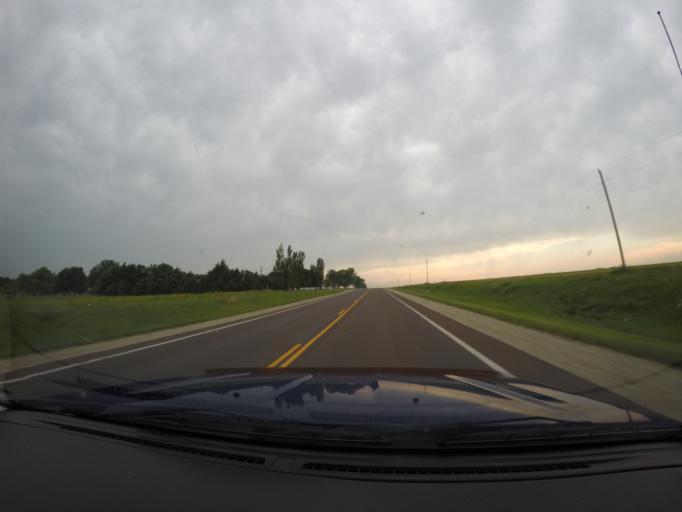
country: US
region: Kansas
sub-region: Riley County
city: Fort Riley North
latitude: 39.3066
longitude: -96.9087
